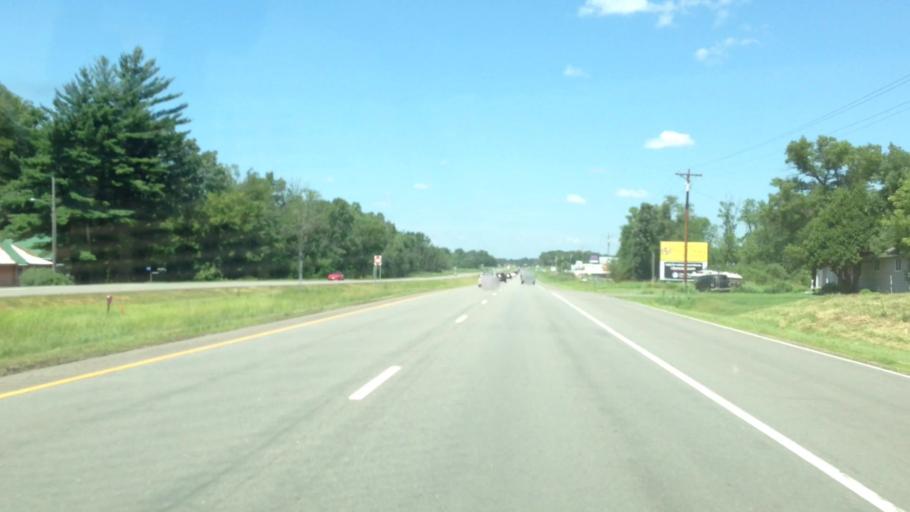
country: US
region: Minnesota
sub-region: Sherburne County
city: Zimmerman
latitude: 45.4247
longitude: -93.5697
